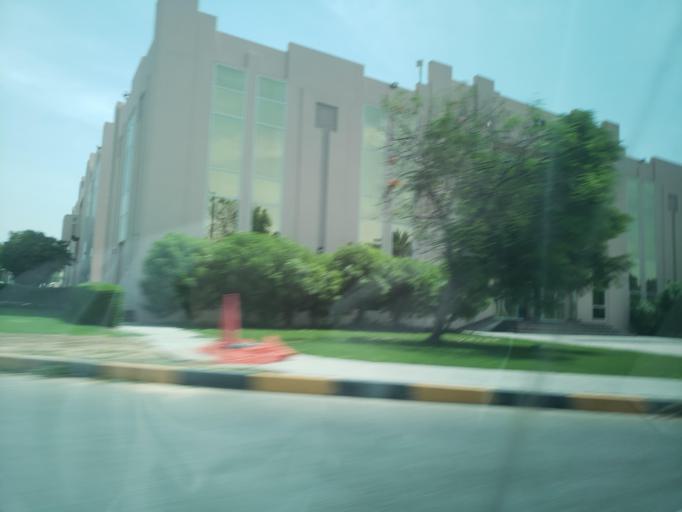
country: AE
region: Ash Shariqah
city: Sharjah
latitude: 25.3300
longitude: 55.4957
